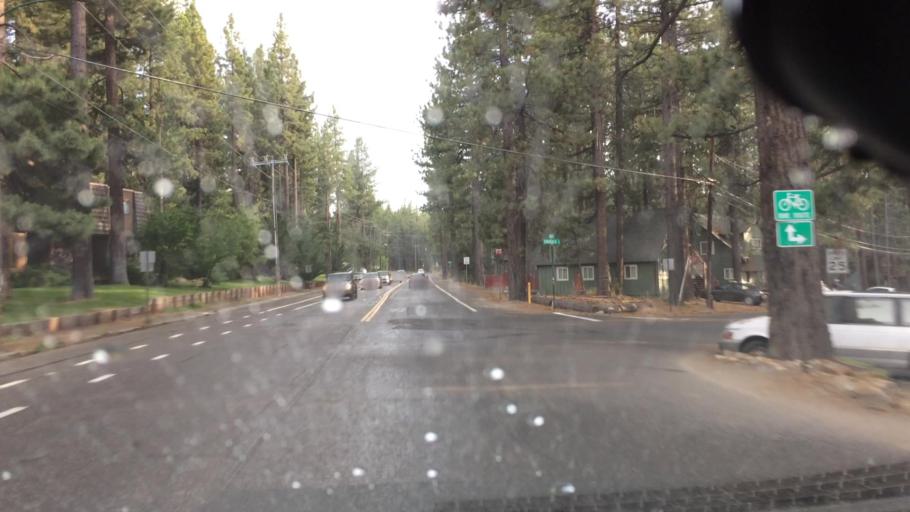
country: US
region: California
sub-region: El Dorado County
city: South Lake Tahoe
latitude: 38.9456
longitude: -119.9500
